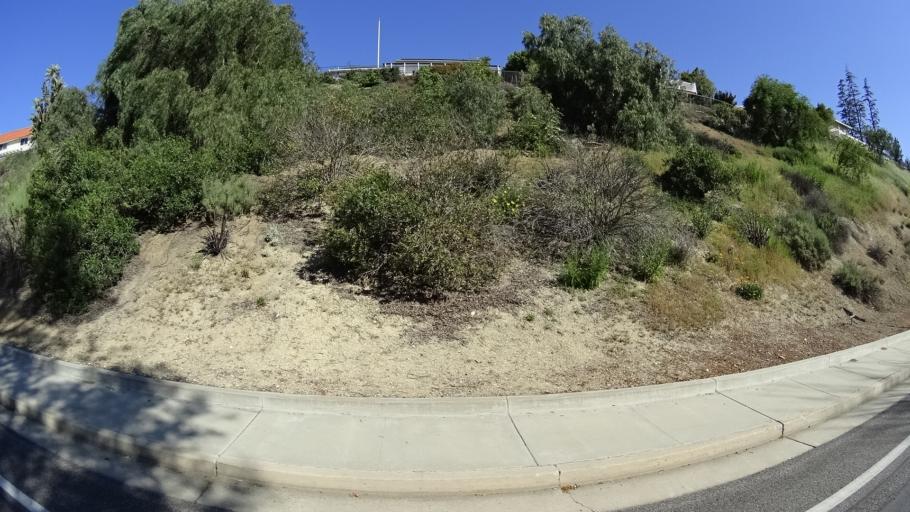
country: US
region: California
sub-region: Ventura County
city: Moorpark
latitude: 34.2368
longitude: -118.8536
